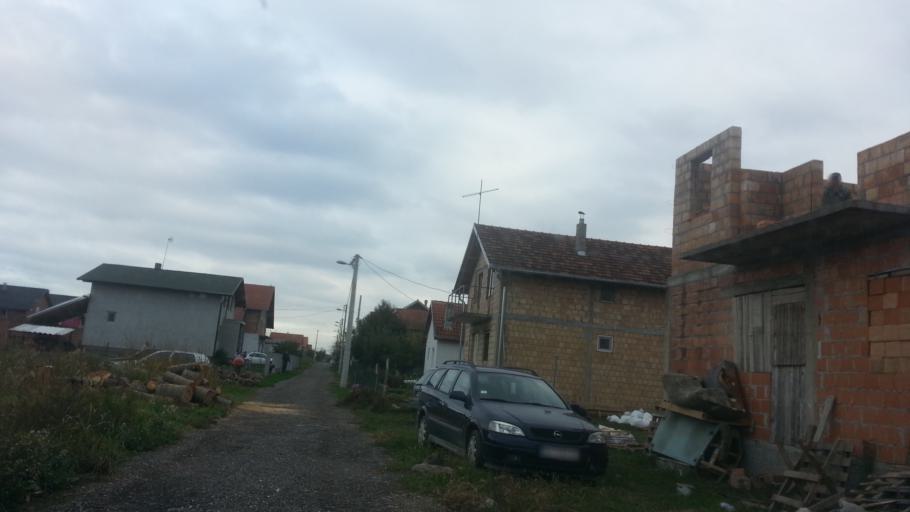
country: RS
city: Novi Banovci
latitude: 44.9204
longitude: 20.2726
